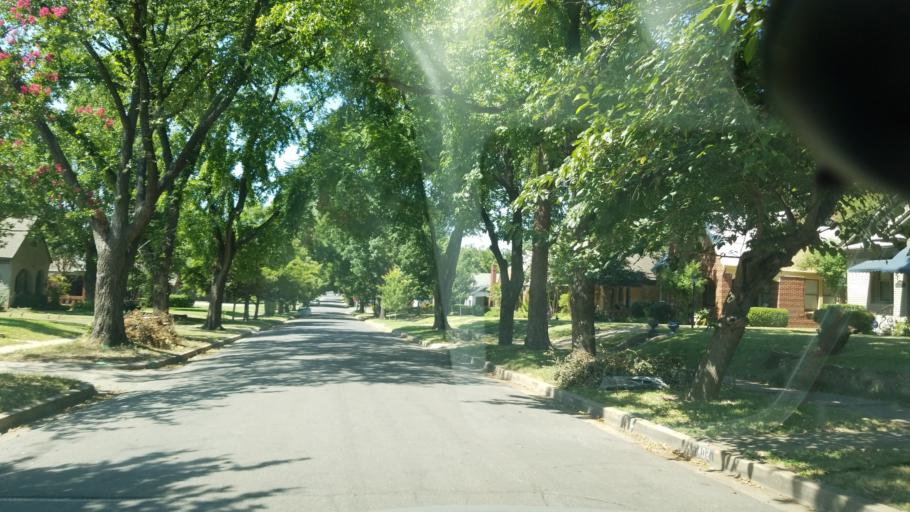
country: US
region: Texas
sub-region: Dallas County
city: Cockrell Hill
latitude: 32.7303
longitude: -96.8556
